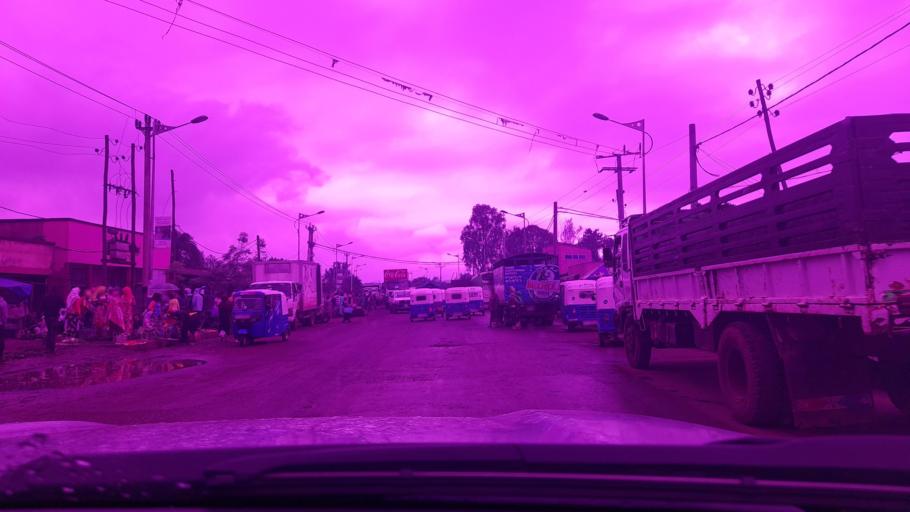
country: ET
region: Oromiya
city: Jima
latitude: 7.6649
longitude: 36.8407
